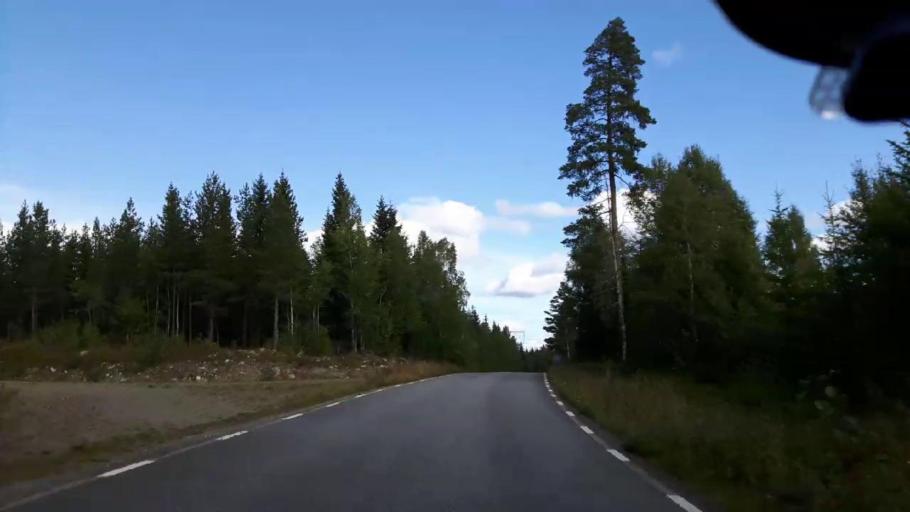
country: SE
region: Jaemtland
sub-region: OEstersunds Kommun
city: Brunflo
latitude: 63.1986
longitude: 15.2232
